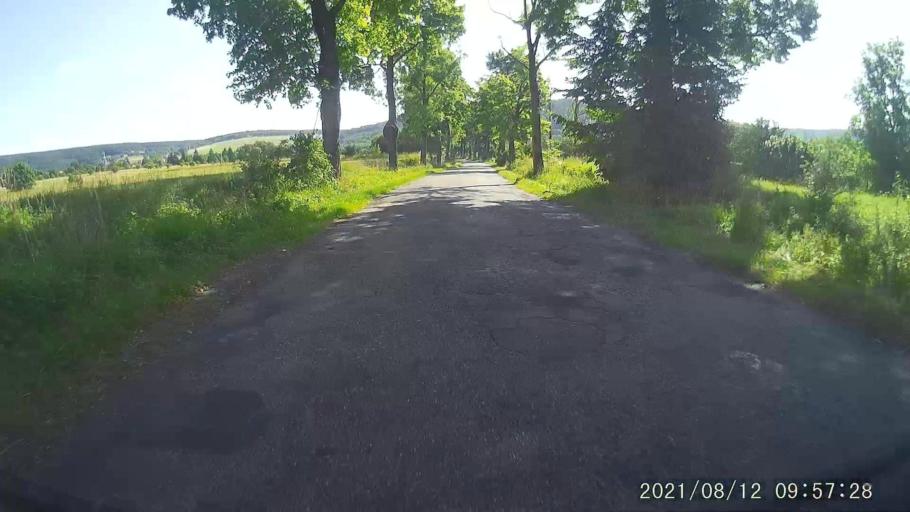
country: PL
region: Lower Silesian Voivodeship
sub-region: Powiat klodzki
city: Szczytna
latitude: 50.4105
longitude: 16.4377
